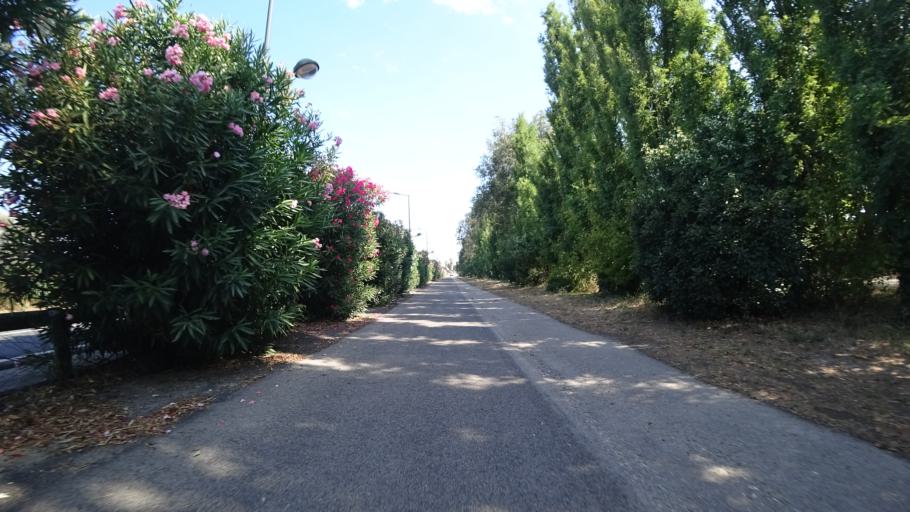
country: FR
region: Languedoc-Roussillon
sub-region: Departement des Pyrenees-Orientales
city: Bompas
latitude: 42.7278
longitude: 2.9252
